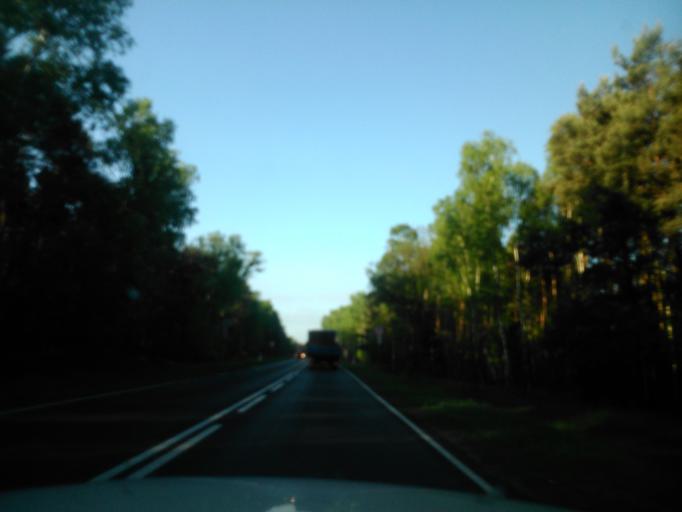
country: PL
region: Masovian Voivodeship
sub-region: Powiat sochaczewski
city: Mlodzieszyn
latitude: 52.3259
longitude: 20.2118
